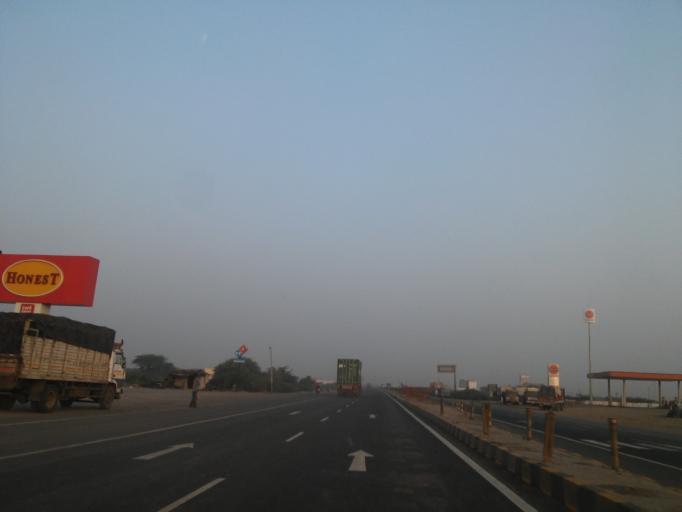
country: IN
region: Gujarat
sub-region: Rajkot
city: Morbi
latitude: 23.0997
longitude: 70.7815
